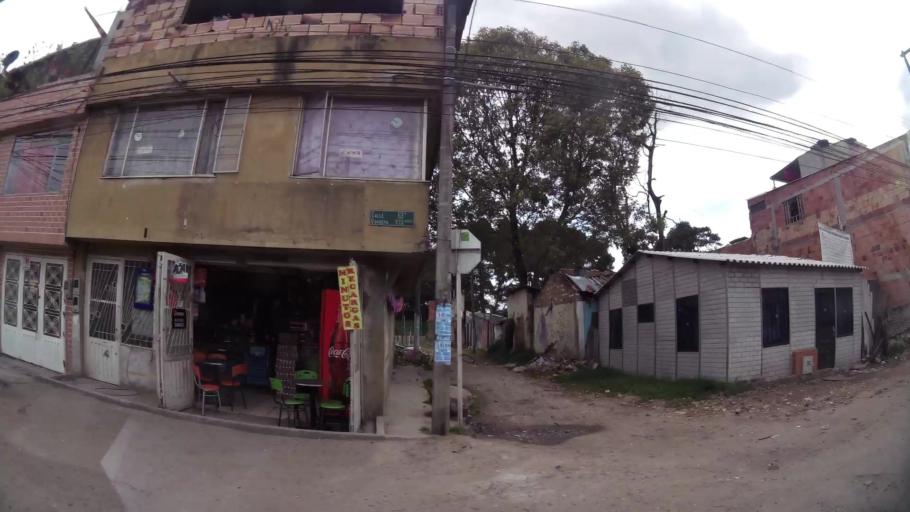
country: CO
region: Cundinamarca
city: Funza
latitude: 4.7085
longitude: -74.1418
